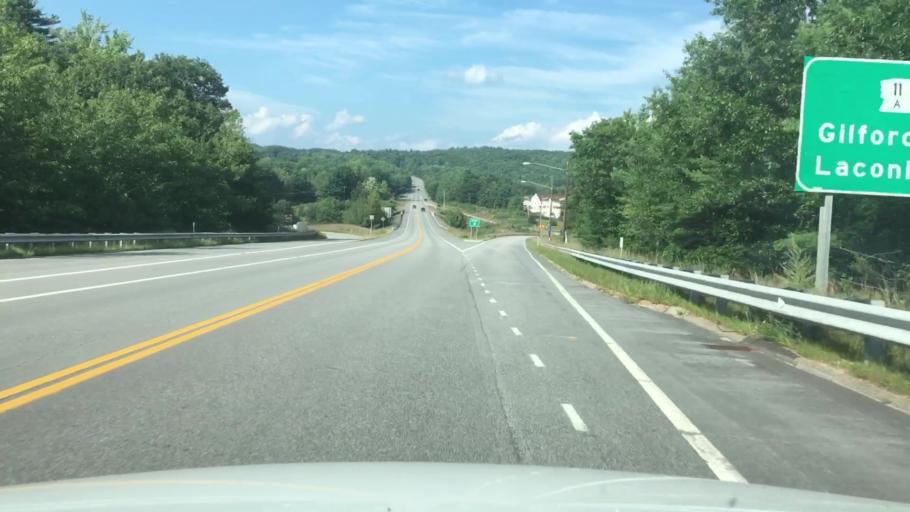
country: US
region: New Hampshire
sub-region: Belknap County
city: Laconia
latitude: 43.5278
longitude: -71.4437
